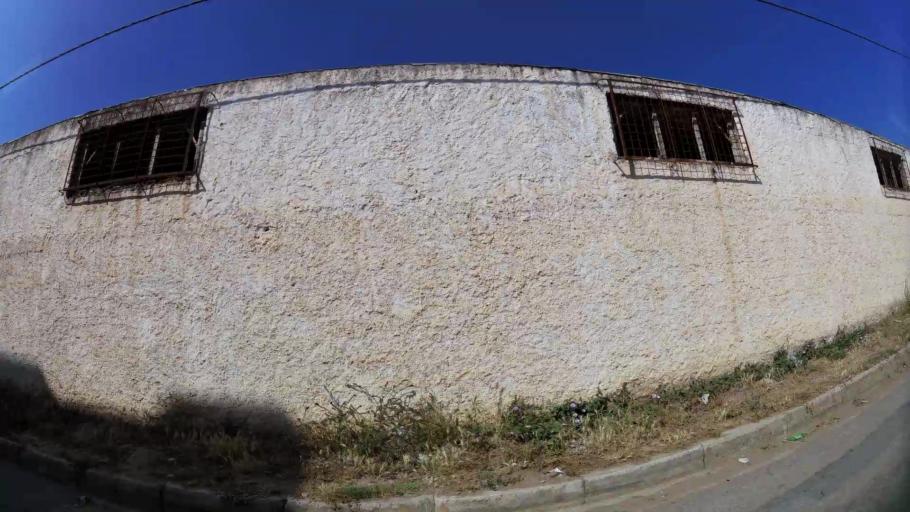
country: MA
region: Rabat-Sale-Zemmour-Zaer
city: Sale
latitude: 34.0742
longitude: -6.7630
